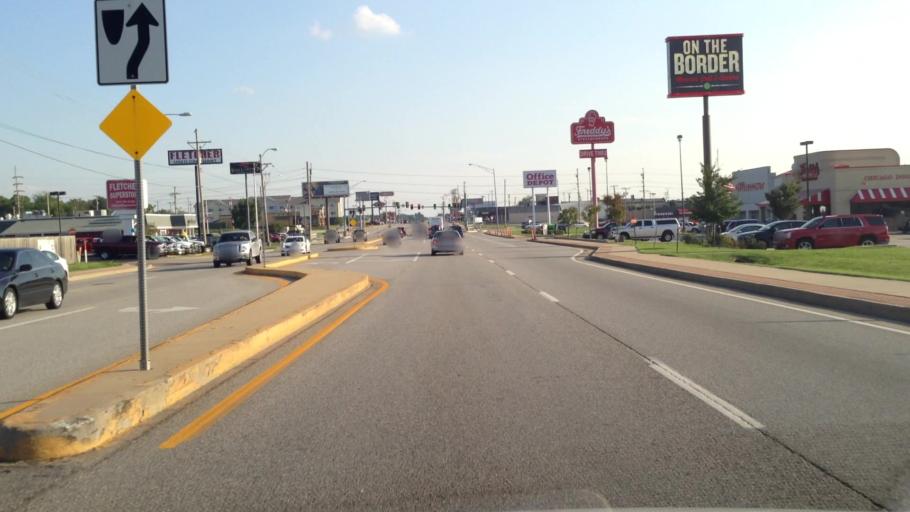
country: US
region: Missouri
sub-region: Jasper County
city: Duquesne
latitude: 37.0571
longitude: -94.4783
